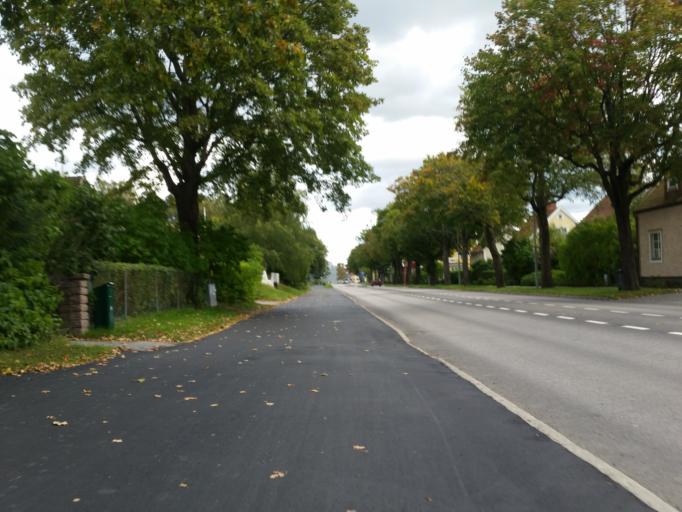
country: SE
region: Stockholm
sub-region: Stockholms Kommun
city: Arsta
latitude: 59.2830
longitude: 18.1020
